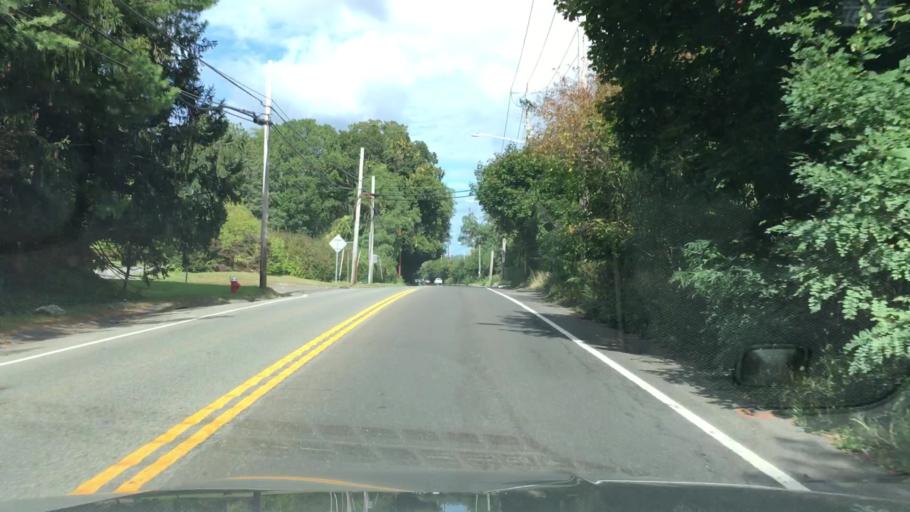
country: US
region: New York
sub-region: Suffolk County
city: Stony Brook
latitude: 40.9171
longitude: -73.1314
